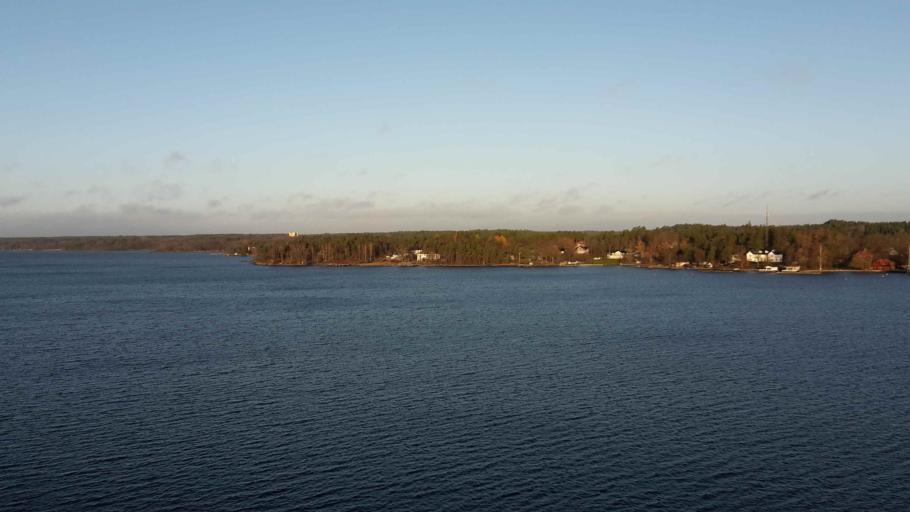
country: SE
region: Stockholm
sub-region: Vaxholms Kommun
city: Vaxholm
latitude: 59.3774
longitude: 18.3297
